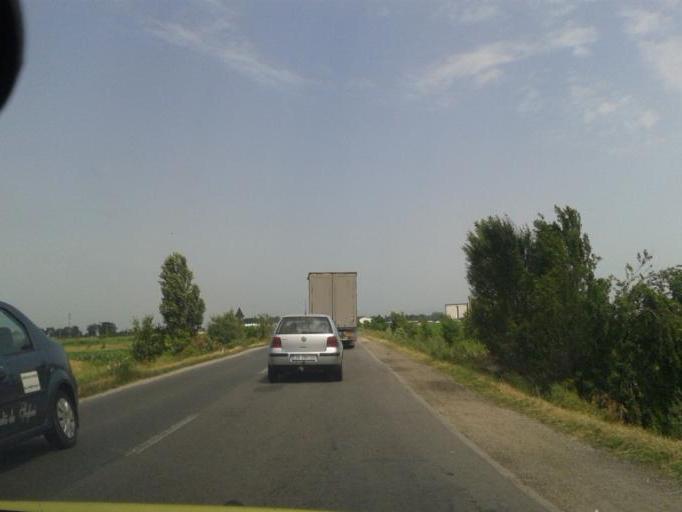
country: RO
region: Dambovita
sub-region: Oras Gaesti
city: Gaesti
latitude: 44.6965
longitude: 25.3118
